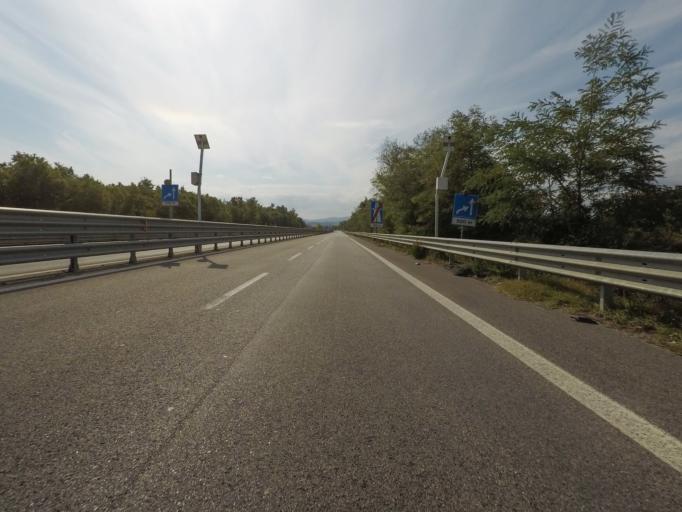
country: IT
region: Tuscany
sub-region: Provincia di Siena
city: Rosia
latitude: 43.2270
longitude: 11.2745
